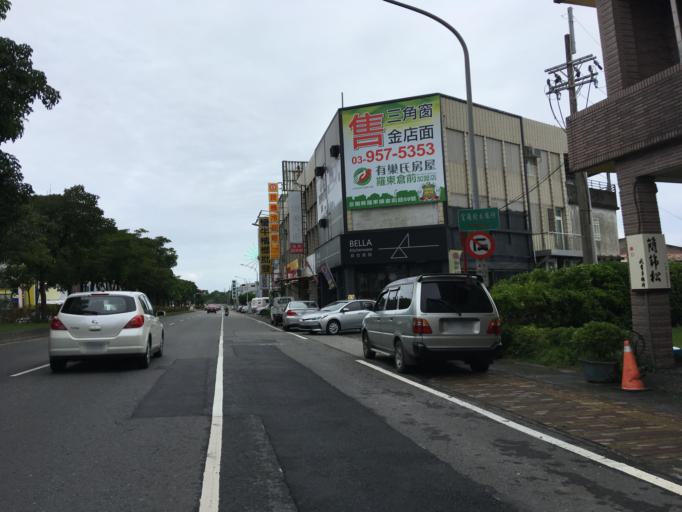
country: TW
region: Taiwan
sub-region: Yilan
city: Yilan
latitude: 24.7076
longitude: 121.7719
